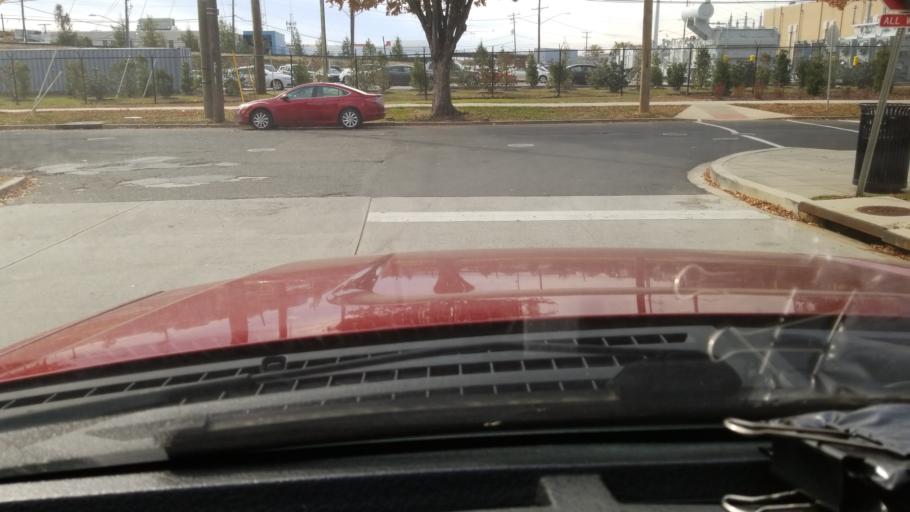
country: US
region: Maryland
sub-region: Prince George's County
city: Colmar Manor
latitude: 38.8984
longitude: -76.9505
